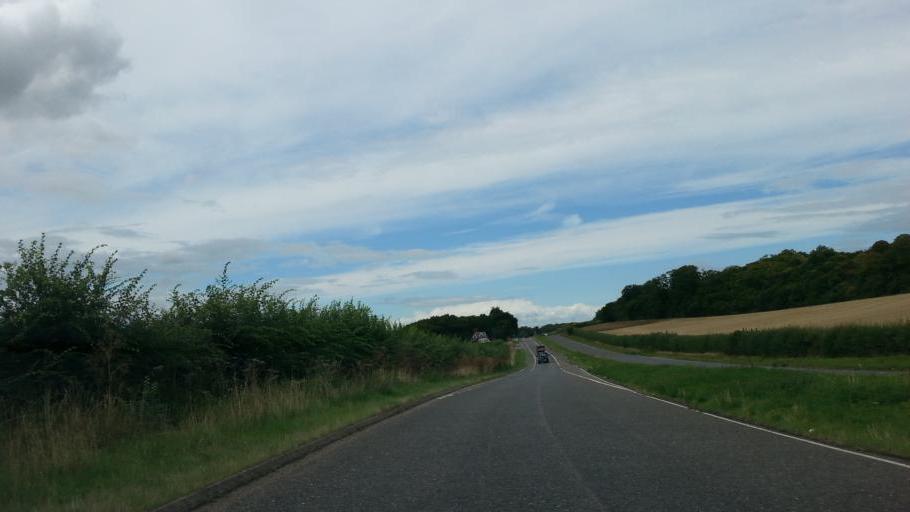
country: GB
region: England
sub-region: Cambridgeshire
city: Sawston
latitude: 52.1305
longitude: 0.2185
